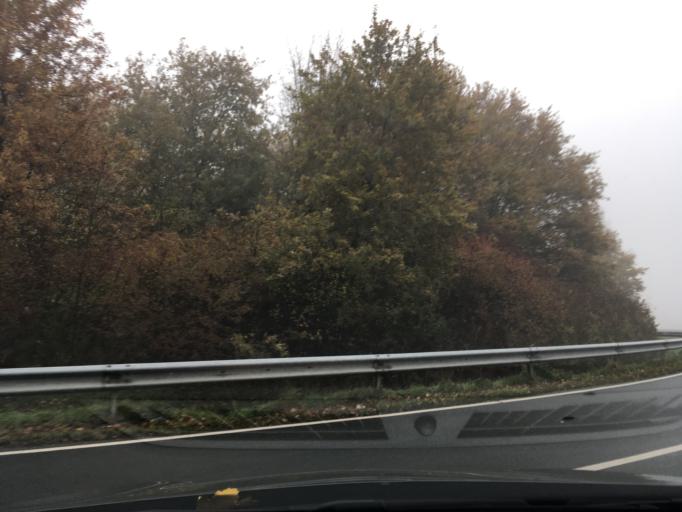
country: DE
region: North Rhine-Westphalia
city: Stadtlohn
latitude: 52.0649
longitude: 6.9277
